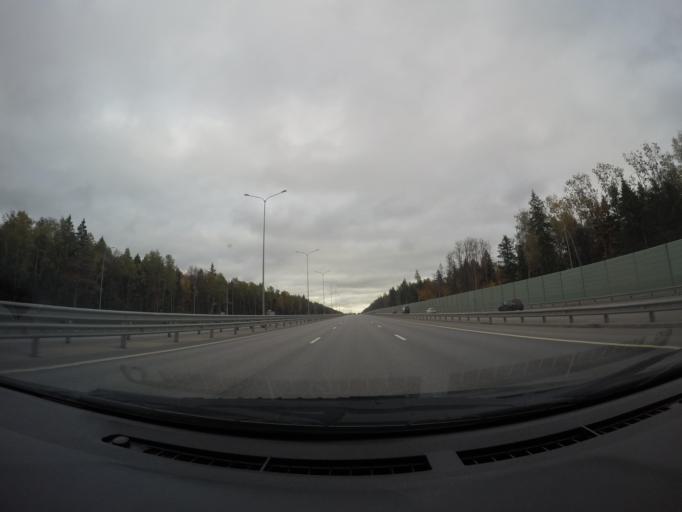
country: RU
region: Moskovskaya
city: Bol'shiye Vyazemy
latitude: 55.5910
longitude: 36.8982
